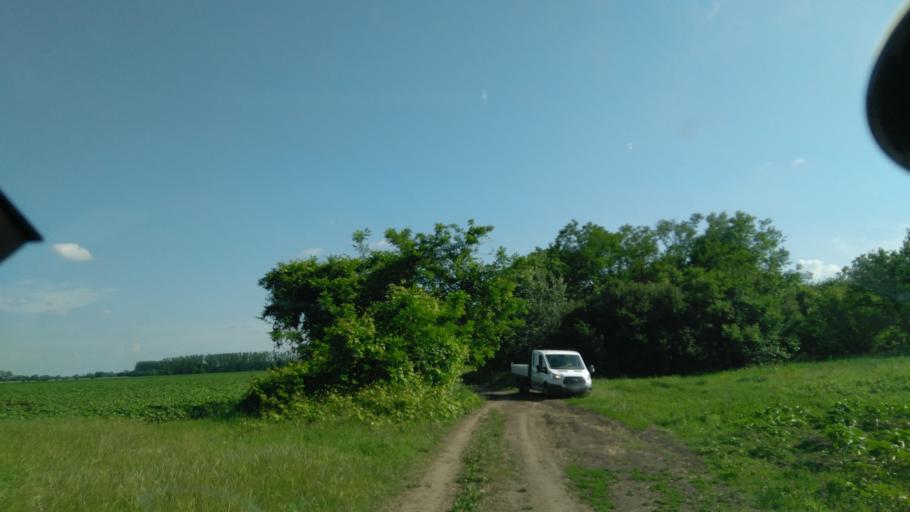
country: HU
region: Bekes
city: Doboz
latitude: 46.7083
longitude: 21.2348
